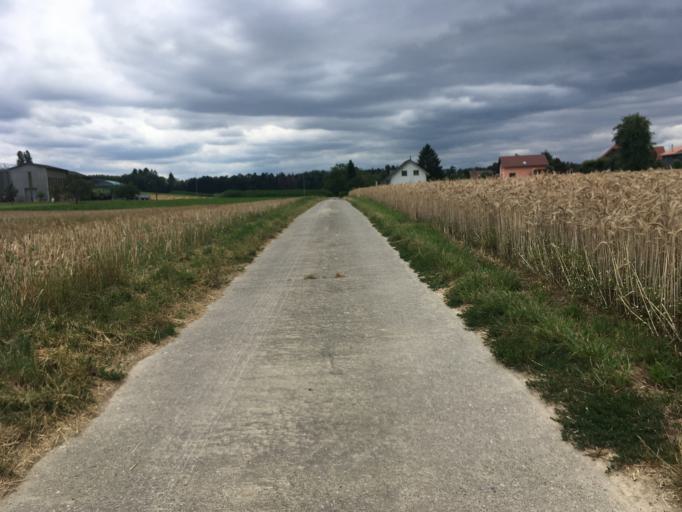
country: CH
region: Vaud
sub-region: Broye-Vully District
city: Payerne
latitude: 46.8728
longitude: 6.9084
